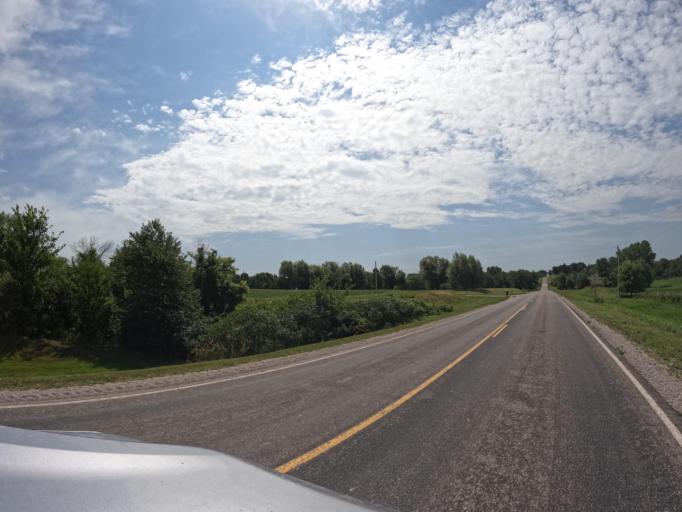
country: US
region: Iowa
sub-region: Appanoose County
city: Centerville
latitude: 40.8000
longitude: -92.9448
